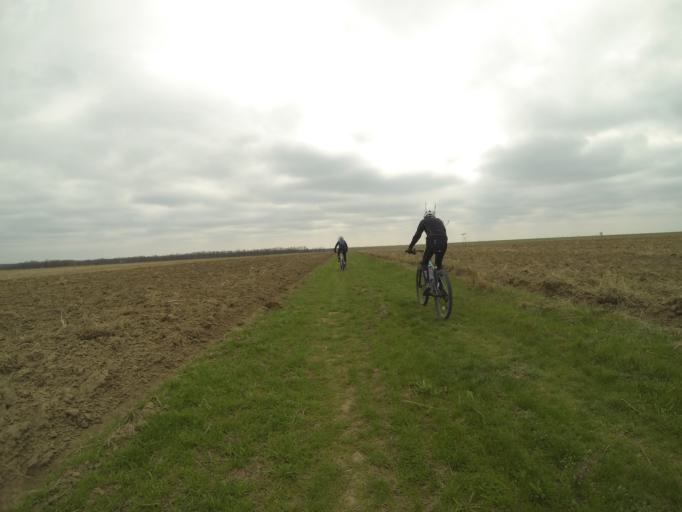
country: RO
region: Dolj
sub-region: Comuna Predesti
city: Predesti
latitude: 44.3215
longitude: 23.6244
